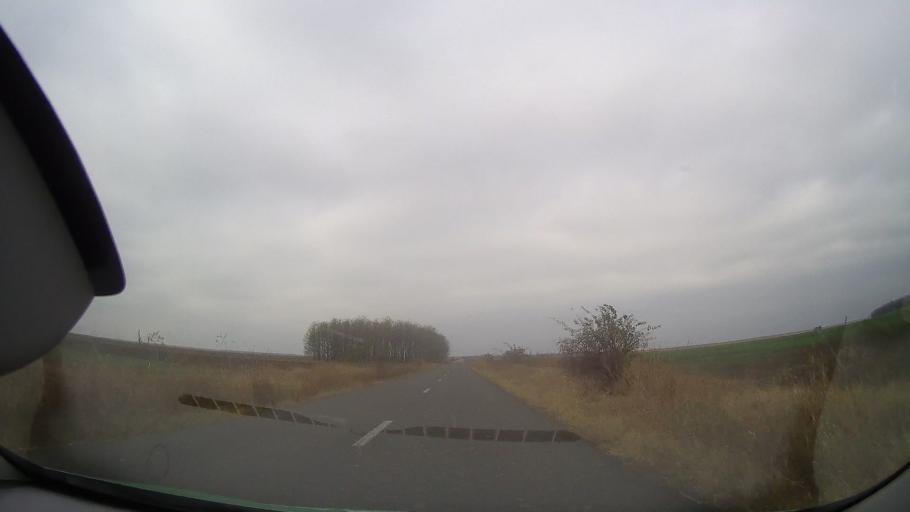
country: RO
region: Buzau
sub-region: Comuna Scutelnici
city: Scutelnici
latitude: 44.8607
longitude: 26.9005
